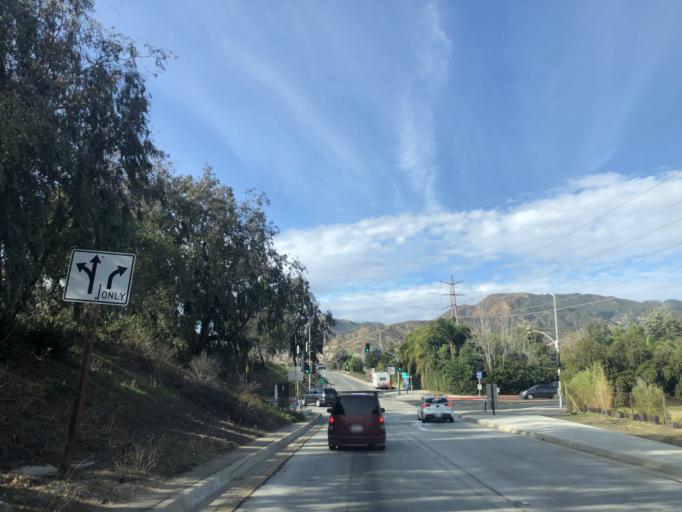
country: US
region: California
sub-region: Los Angeles County
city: San Fernando
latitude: 34.3162
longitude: -118.4388
